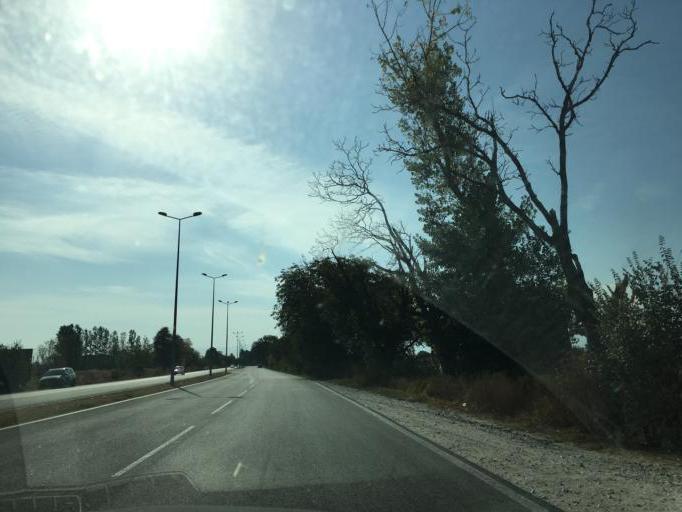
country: BG
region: Pazardzhik
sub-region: Obshtina Pazardzhik
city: Pazardzhik
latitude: 42.2209
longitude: 24.3120
